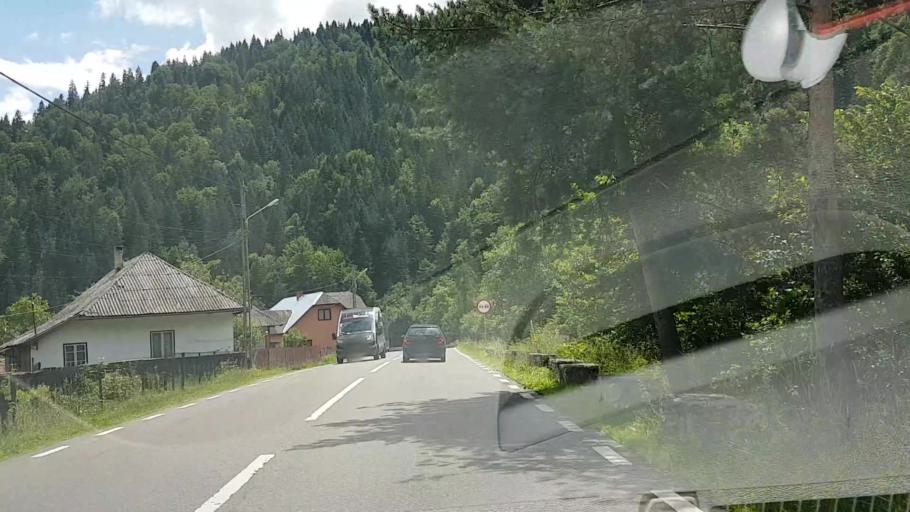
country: RO
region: Suceava
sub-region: Comuna Brosteni
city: Brosteni
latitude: 47.2579
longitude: 25.6697
